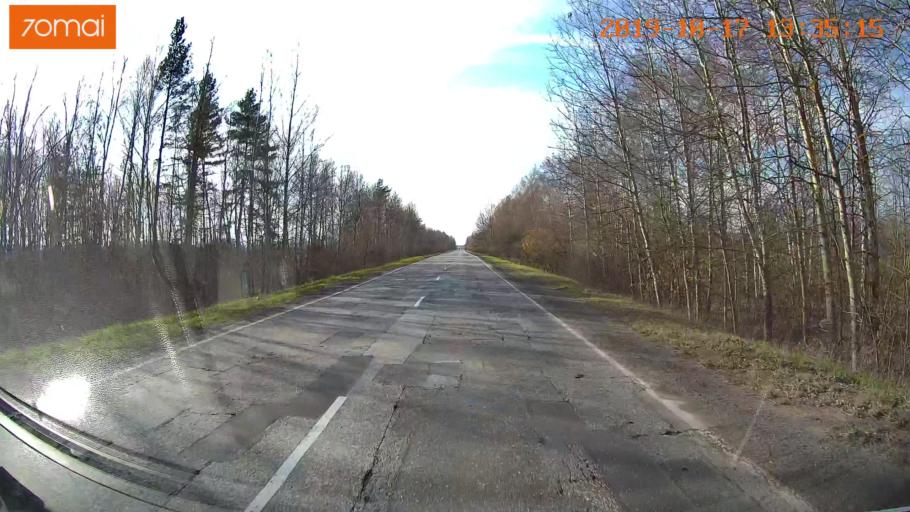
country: RU
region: Vladimir
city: Velikodvorskiy
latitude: 55.1431
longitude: 40.6944
